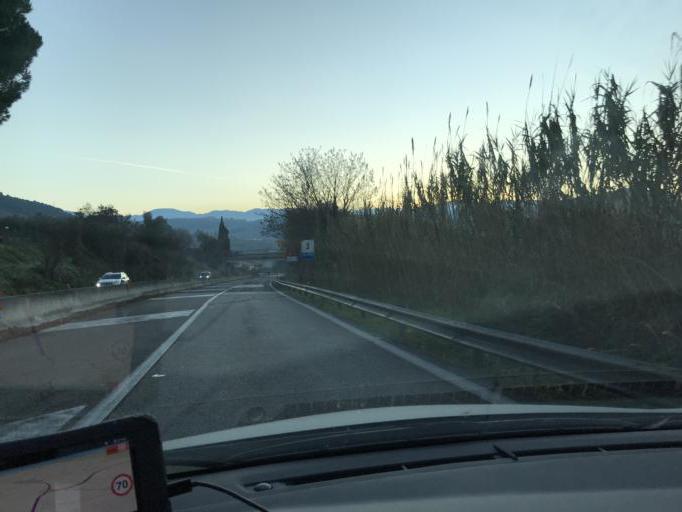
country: IT
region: Umbria
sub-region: Provincia di Terni
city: Terni
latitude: 42.5858
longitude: 12.6672
